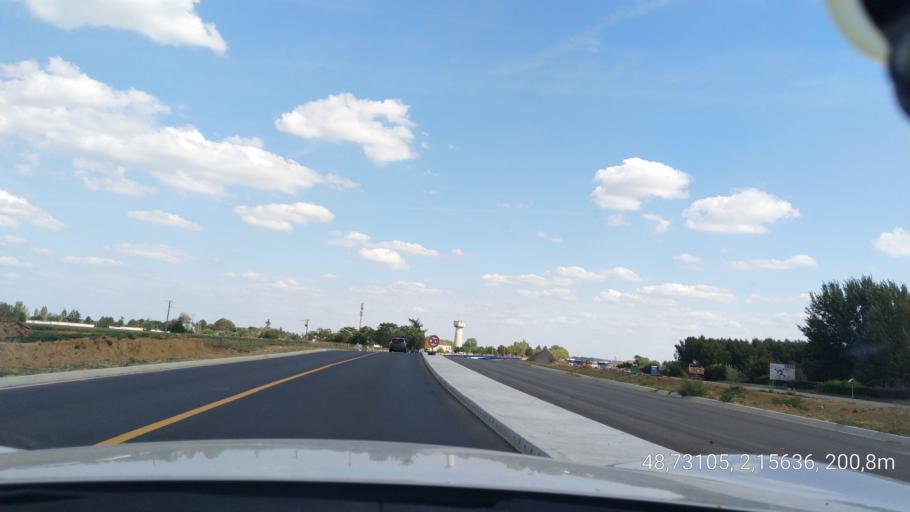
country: FR
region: Ile-de-France
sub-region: Departement de l'Essonne
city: Saclay
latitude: 48.7304
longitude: 2.1560
